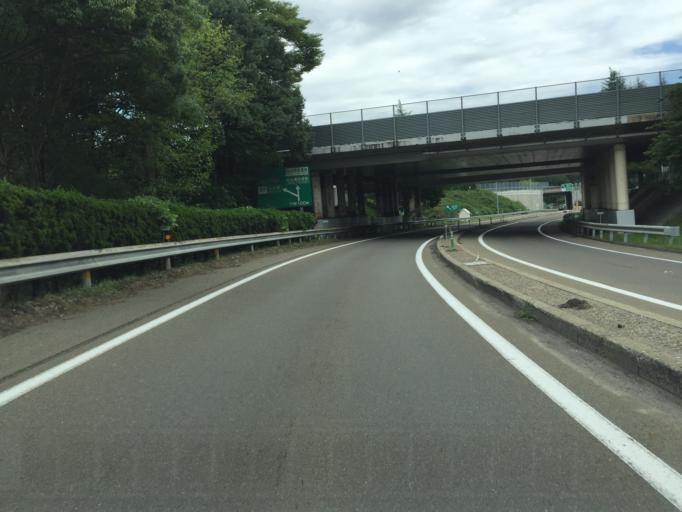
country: JP
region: Miyagi
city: Sendai
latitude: 38.2150
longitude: 140.8028
